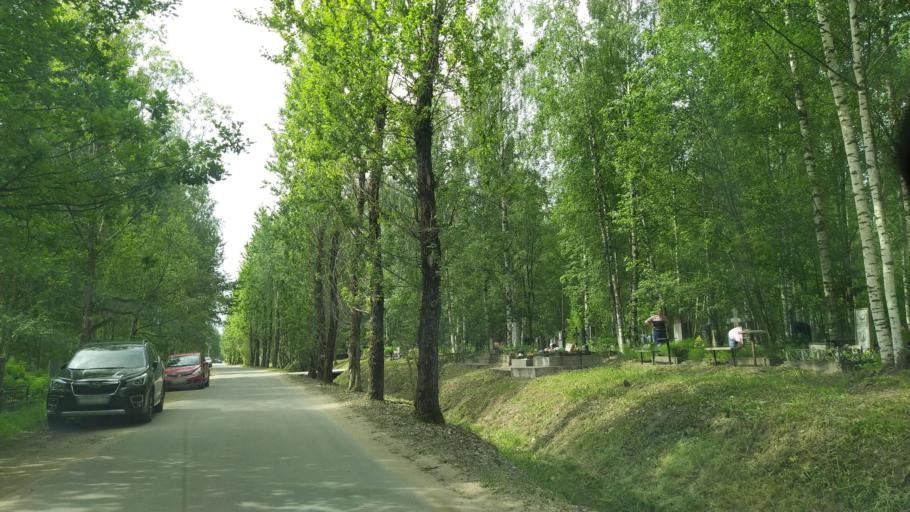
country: RU
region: St.-Petersburg
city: Dachnoye
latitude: 59.7701
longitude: 30.2649
